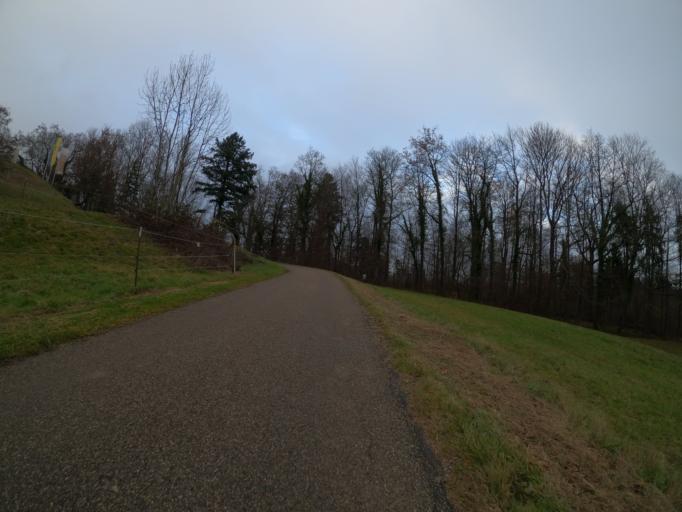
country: DE
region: Baden-Wuerttemberg
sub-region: Regierungsbezirk Stuttgart
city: Waschenbeuren
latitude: 48.7667
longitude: 9.7069
